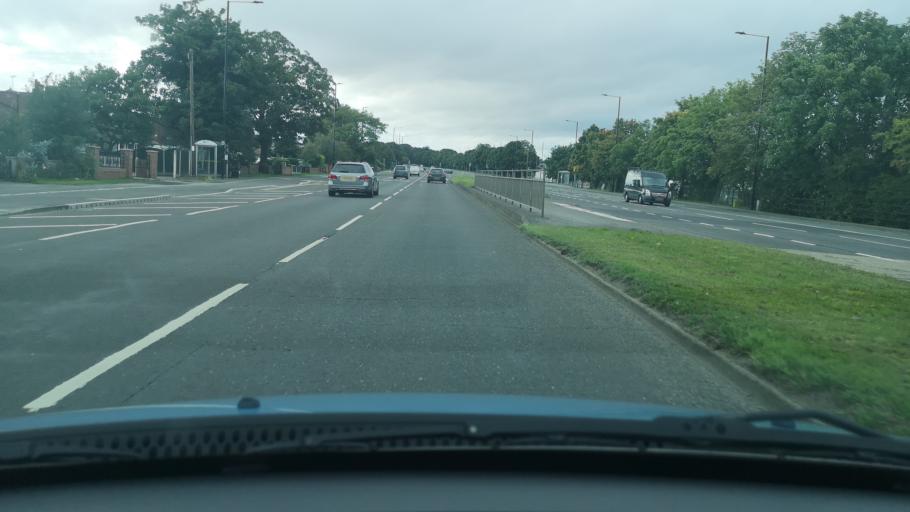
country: GB
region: England
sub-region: Doncaster
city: Bentley
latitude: 53.5403
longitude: -1.1682
